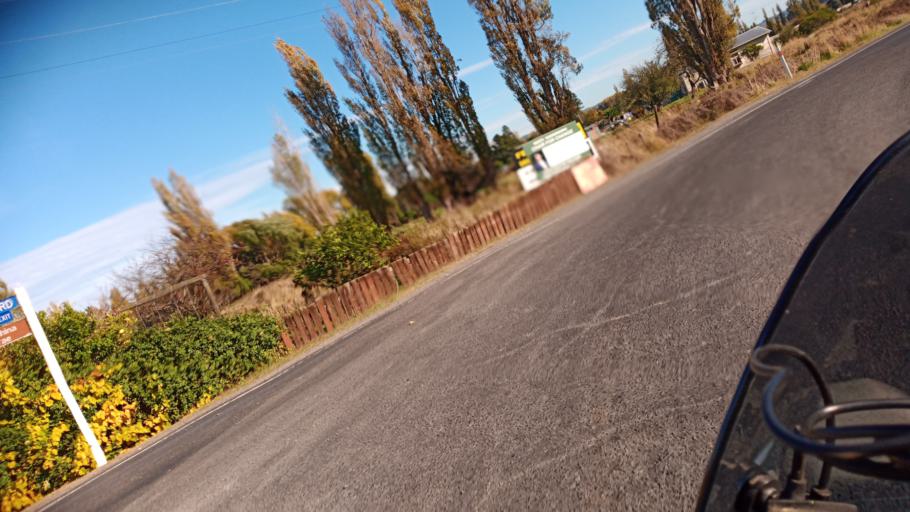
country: NZ
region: Hawke's Bay
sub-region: Wairoa District
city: Wairoa
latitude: -39.0294
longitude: 177.4370
